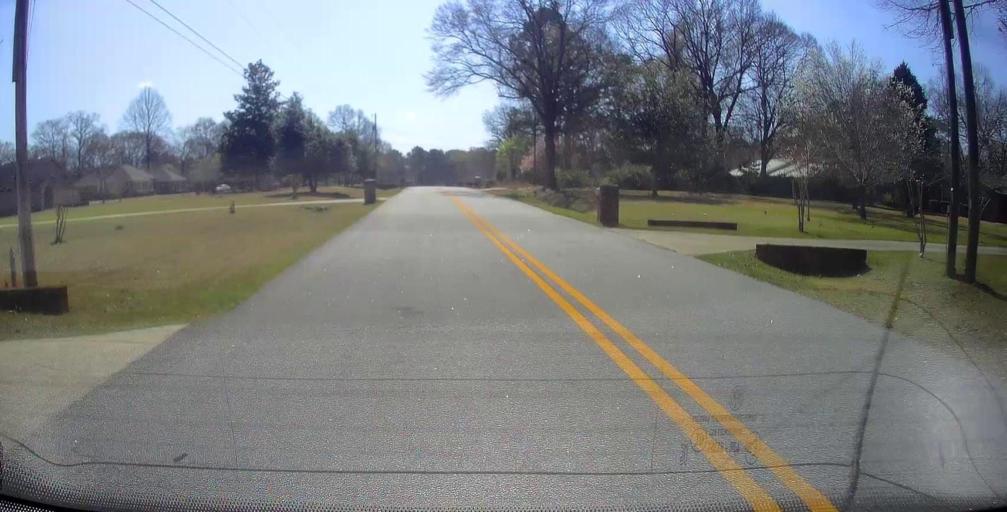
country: US
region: Georgia
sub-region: Houston County
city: Centerville
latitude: 32.5890
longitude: -83.6918
